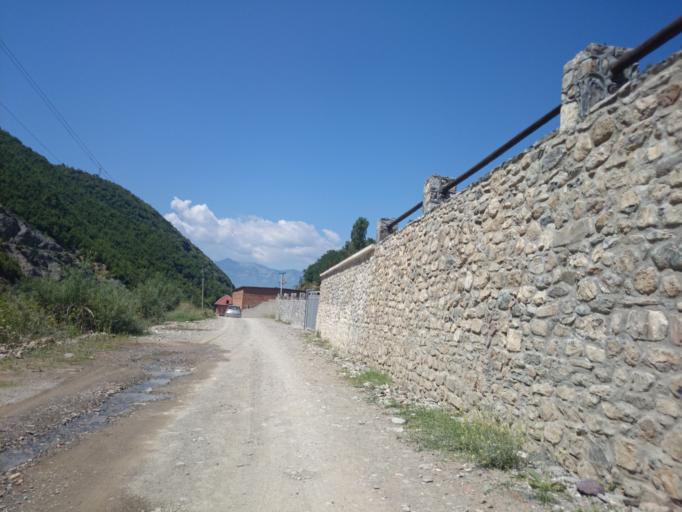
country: AL
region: Diber
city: Peshkopi
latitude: 41.6854
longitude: 20.4556
